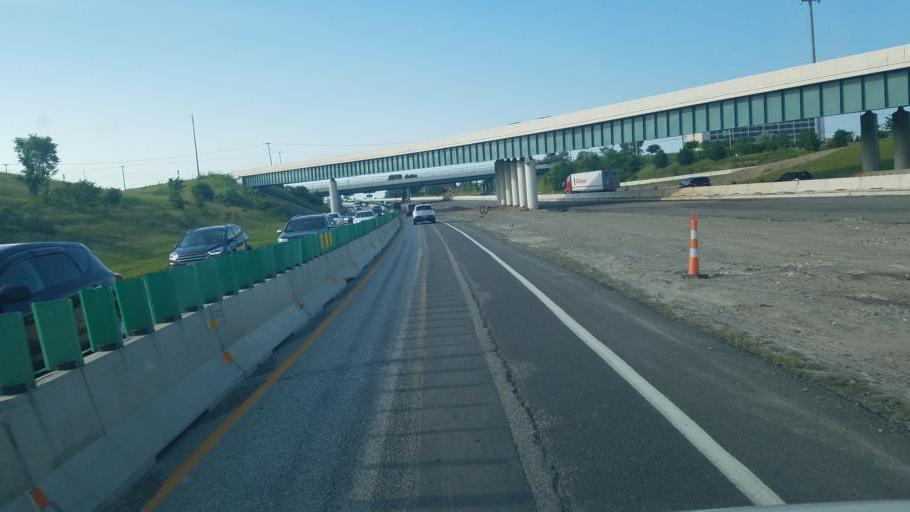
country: US
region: Ohio
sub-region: Cuyahoga County
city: Bedford Heights
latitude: 41.4071
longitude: -81.5067
